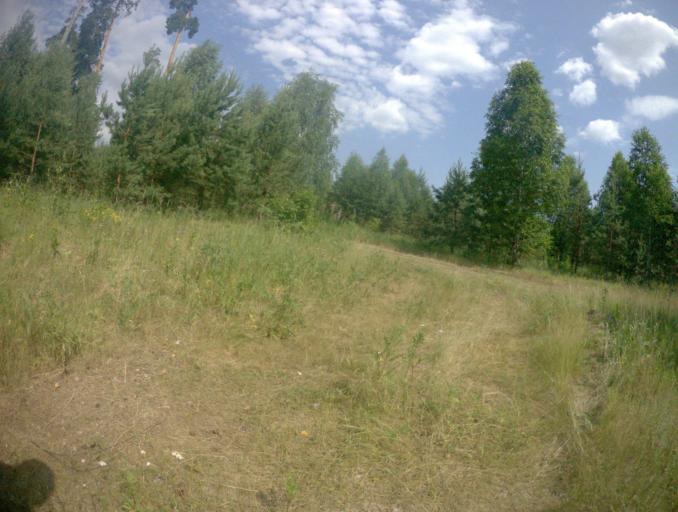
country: RU
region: Ivanovo
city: Talitsy
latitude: 56.3853
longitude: 42.2862
